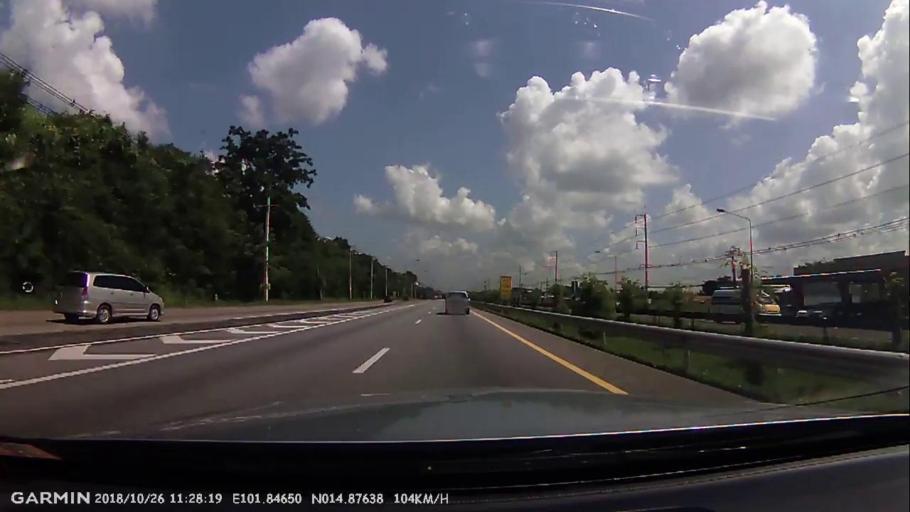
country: TH
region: Nakhon Ratchasima
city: Sung Noen
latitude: 14.8771
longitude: 101.8464
